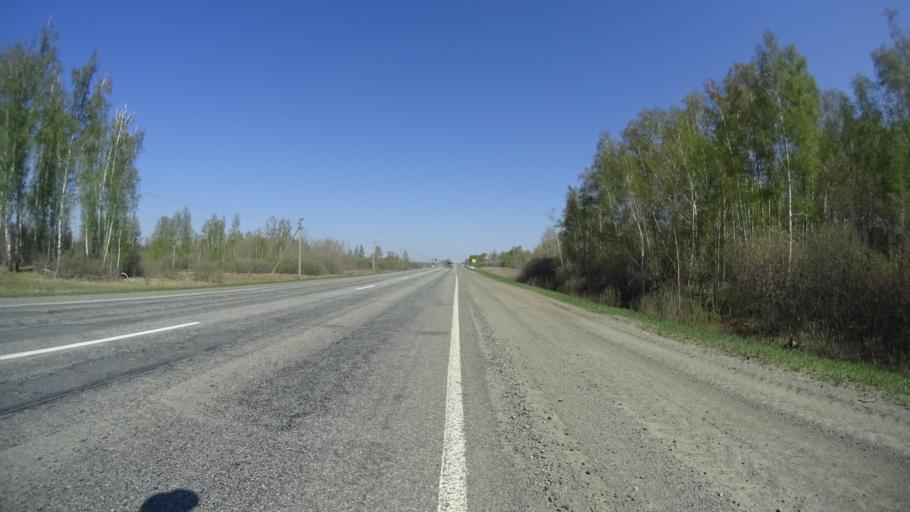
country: RU
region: Chelyabinsk
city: Troitsk
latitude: 54.1845
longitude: 61.4343
